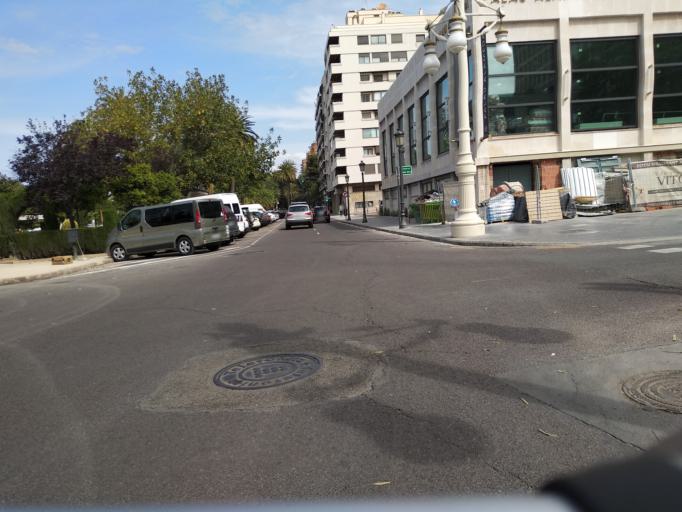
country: ES
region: Valencia
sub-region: Provincia de Valencia
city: Valencia
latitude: 39.4723
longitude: -0.3629
